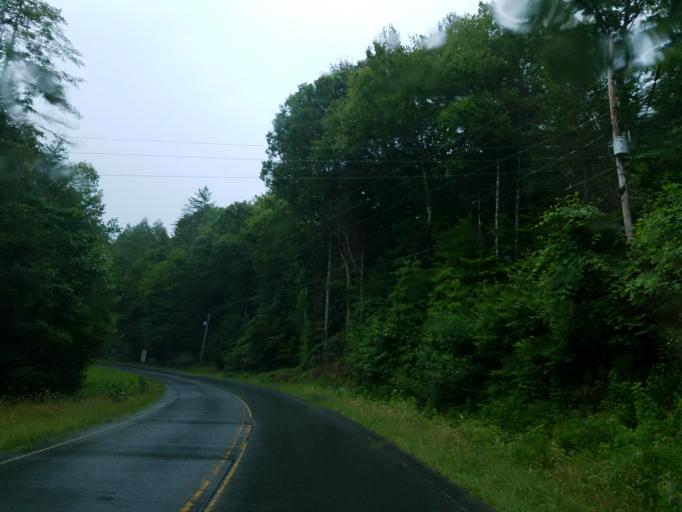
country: US
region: Georgia
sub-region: Fannin County
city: Blue Ridge
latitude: 34.7819
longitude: -84.2625
